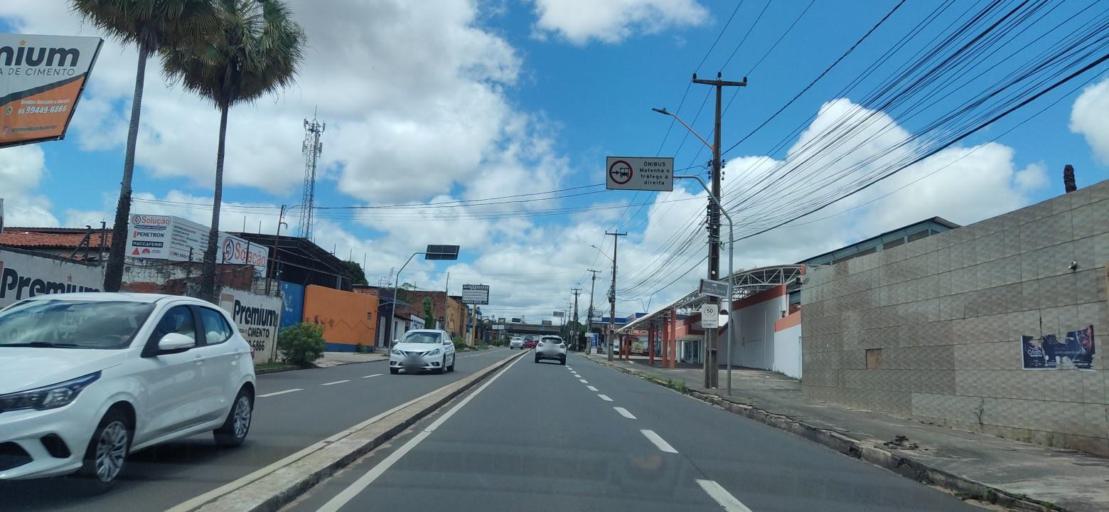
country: BR
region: Piaui
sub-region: Teresina
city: Teresina
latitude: -5.0885
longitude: -42.7630
